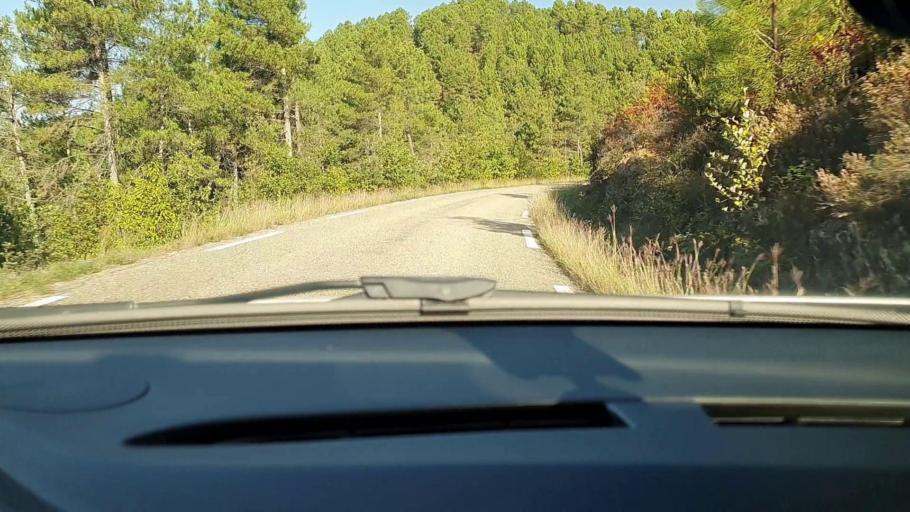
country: FR
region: Languedoc-Roussillon
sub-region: Departement du Gard
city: Besseges
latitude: 44.3221
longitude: 4.0752
